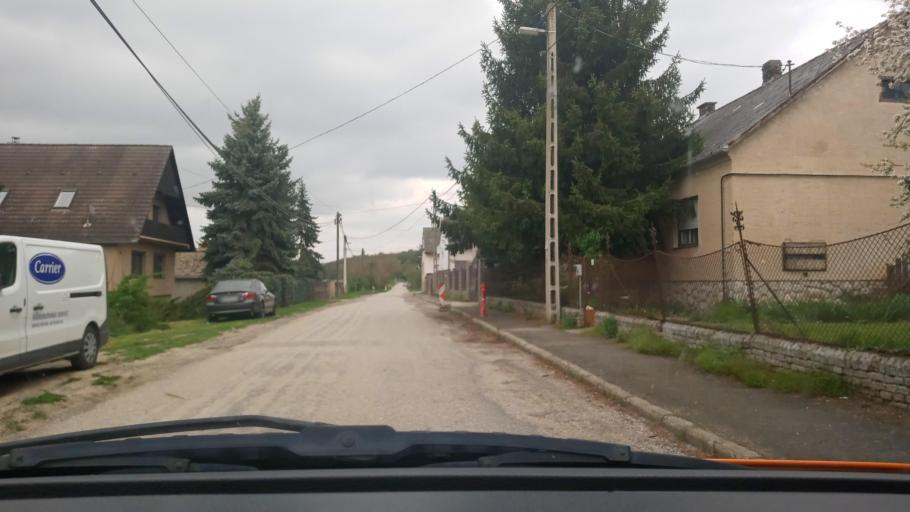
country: HU
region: Baranya
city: Boly
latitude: 46.0079
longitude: 18.5482
